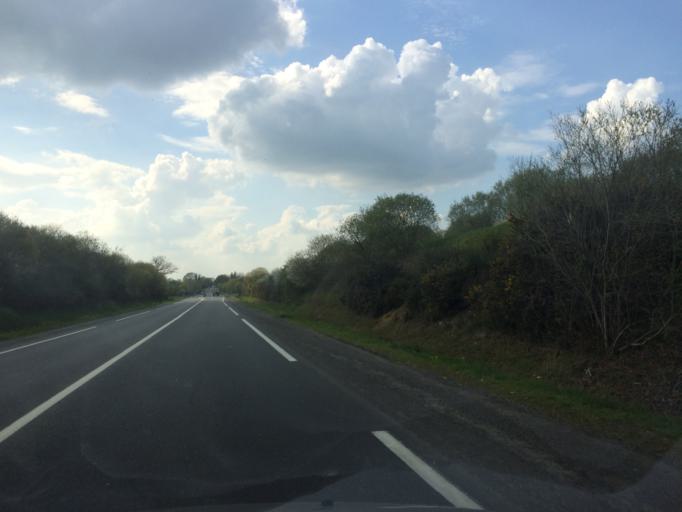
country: FR
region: Pays de la Loire
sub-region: Departement de la Loire-Atlantique
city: Blain
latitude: 47.4692
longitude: -1.7271
